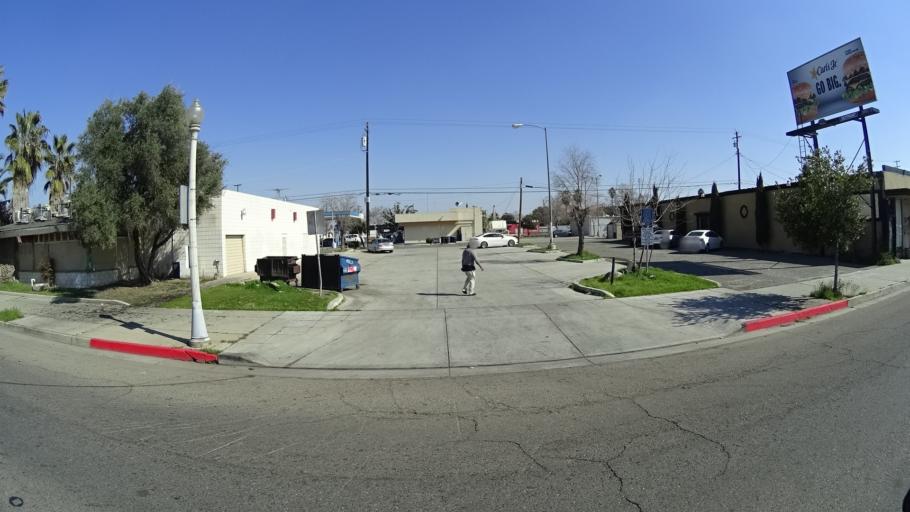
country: US
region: California
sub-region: Fresno County
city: Fresno
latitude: 36.7500
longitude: -119.7906
